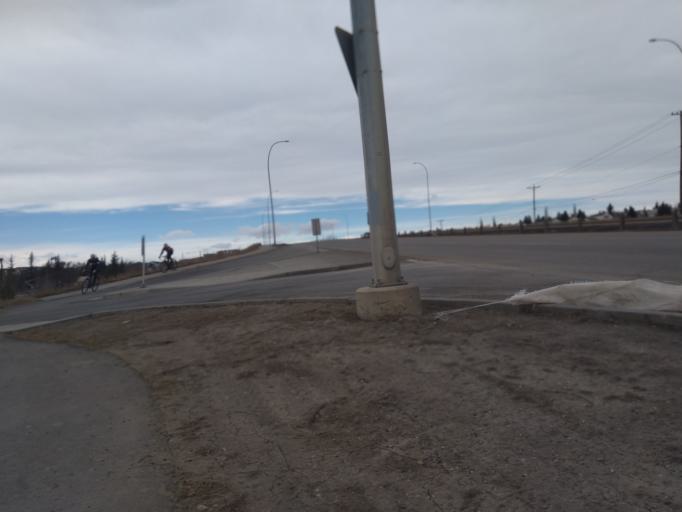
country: CA
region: Alberta
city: Calgary
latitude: 51.1542
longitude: -114.0364
